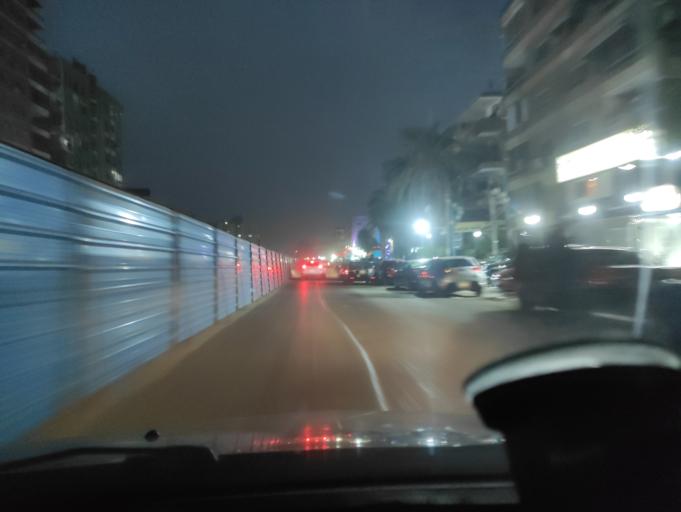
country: EG
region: Muhafazat al Qahirah
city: Cairo
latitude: 30.0438
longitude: 31.3305
